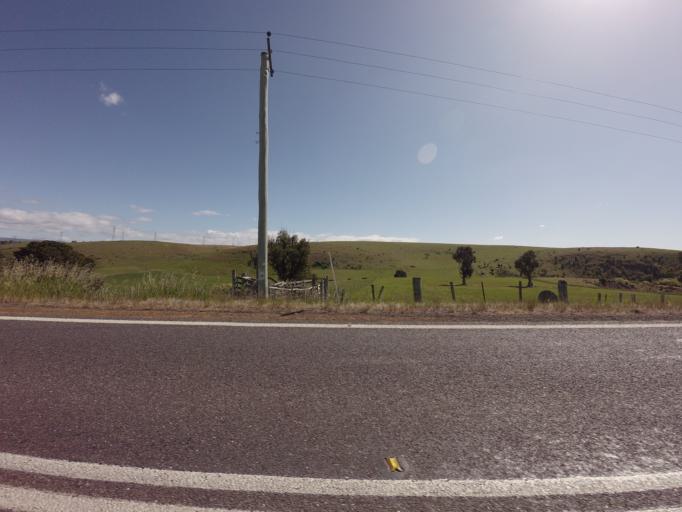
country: AU
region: Tasmania
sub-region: Derwent Valley
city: New Norfolk
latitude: -42.6560
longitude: 146.9350
